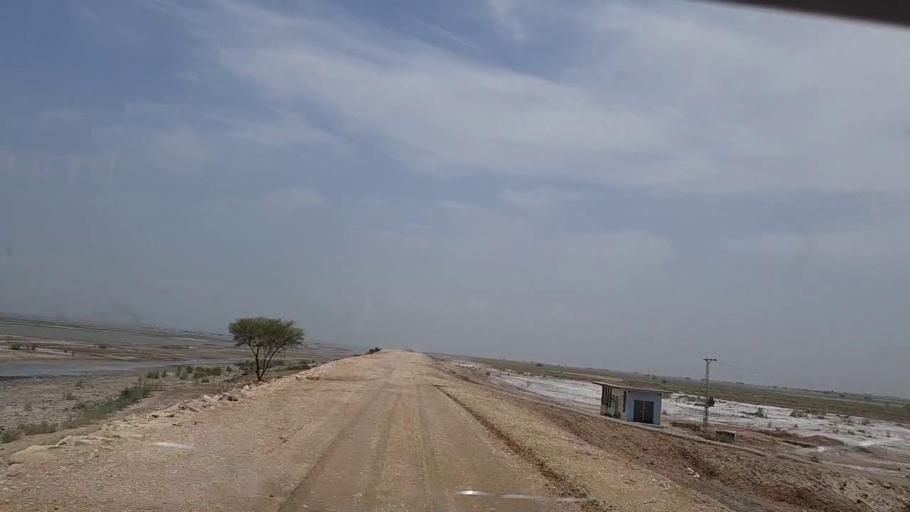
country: PK
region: Sindh
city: Sehwan
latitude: 26.4159
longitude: 67.7553
